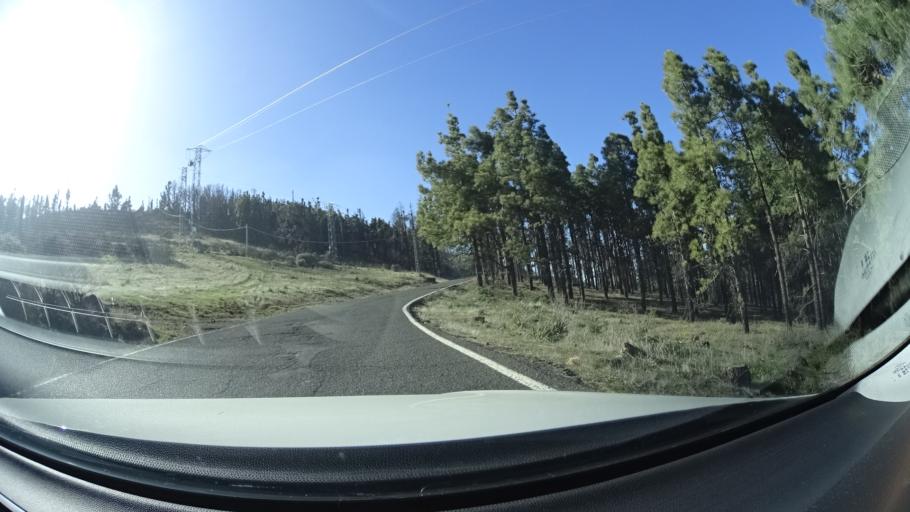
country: ES
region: Canary Islands
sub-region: Provincia de Las Palmas
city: San Bartolome
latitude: 27.9667
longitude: -15.5612
